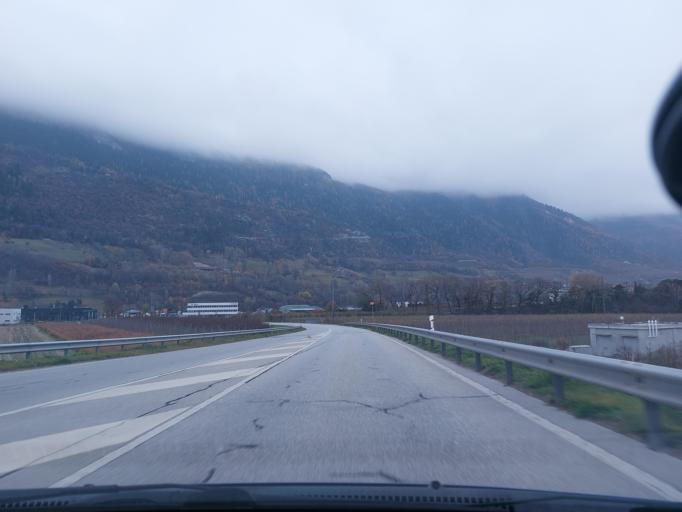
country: CH
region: Valais
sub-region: Sierre District
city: Chalais
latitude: 46.2769
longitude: 7.5160
